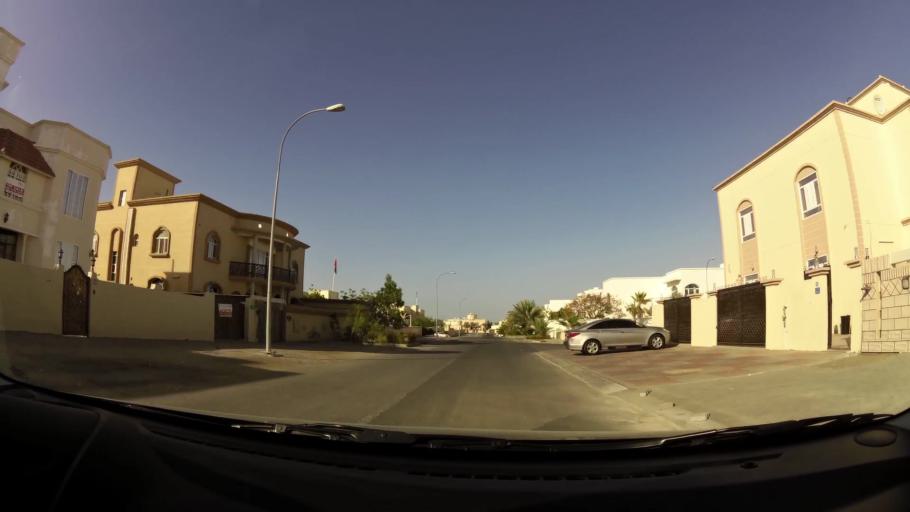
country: OM
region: Muhafazat Masqat
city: As Sib al Jadidah
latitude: 23.6017
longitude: 58.2075
